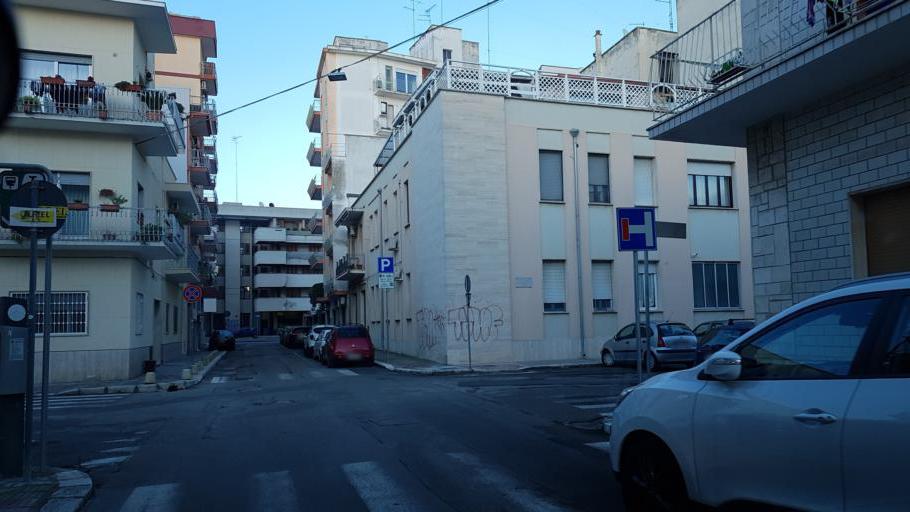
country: IT
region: Apulia
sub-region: Provincia di Lecce
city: Lecce
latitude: 40.3613
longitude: 18.1777
